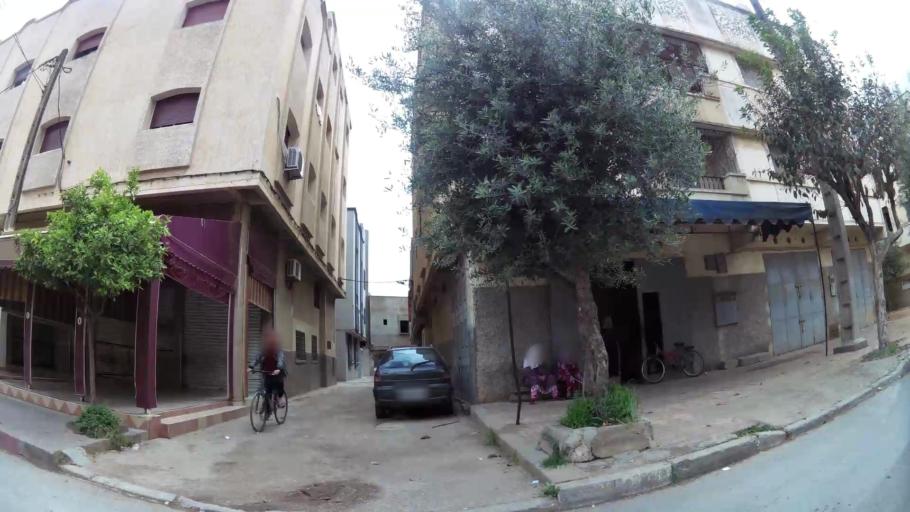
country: MA
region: Rabat-Sale-Zemmour-Zaer
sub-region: Khemisset
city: Tiflet
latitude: 33.8928
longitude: -6.3215
